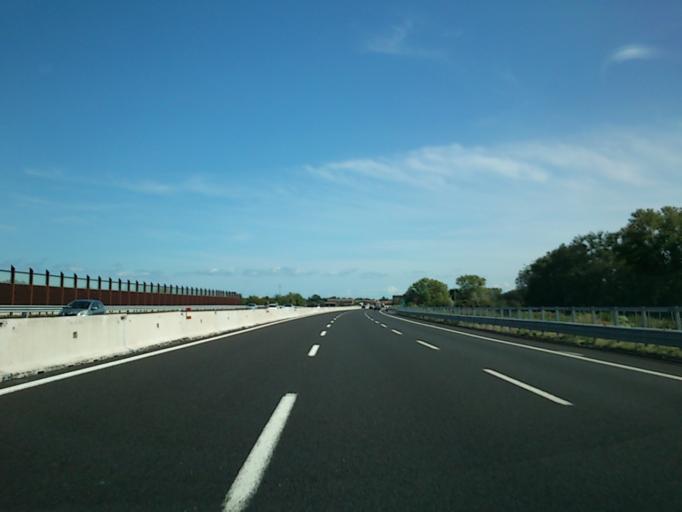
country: IT
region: The Marches
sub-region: Provincia di Pesaro e Urbino
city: Centinarola
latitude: 43.8399
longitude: 12.9822
